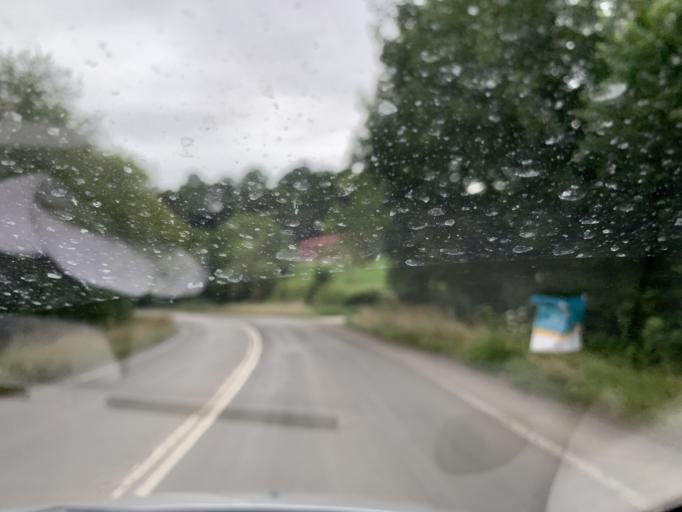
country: ES
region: Asturias
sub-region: Province of Asturias
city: Amieva
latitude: 43.3386
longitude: -5.0098
